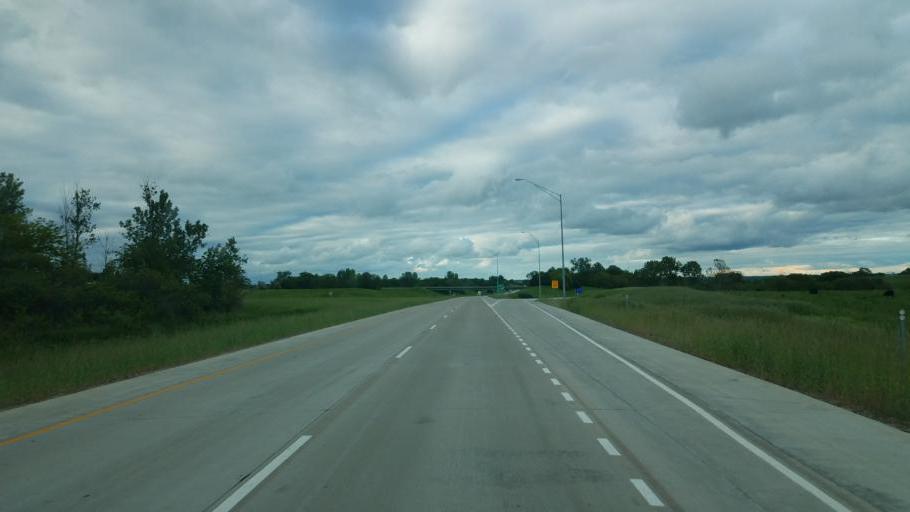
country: US
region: Iowa
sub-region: Decatur County
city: Lamoni
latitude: 40.6187
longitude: -93.8940
